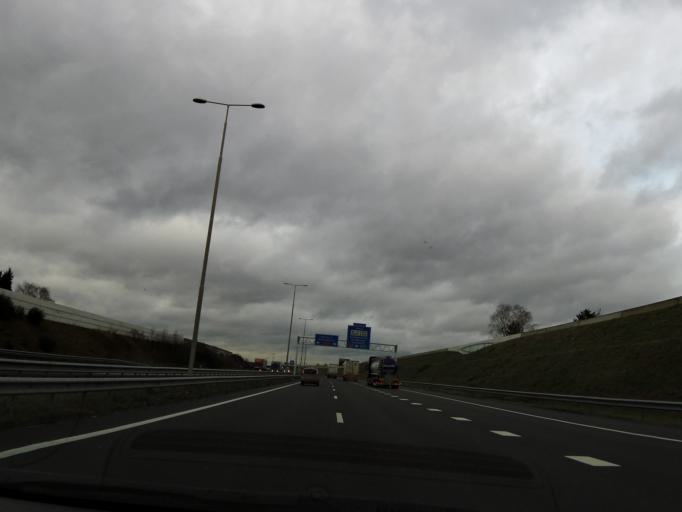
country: NL
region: Limburg
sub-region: Gemeente Venlo
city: Tegelen
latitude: 51.3719
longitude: 6.1231
